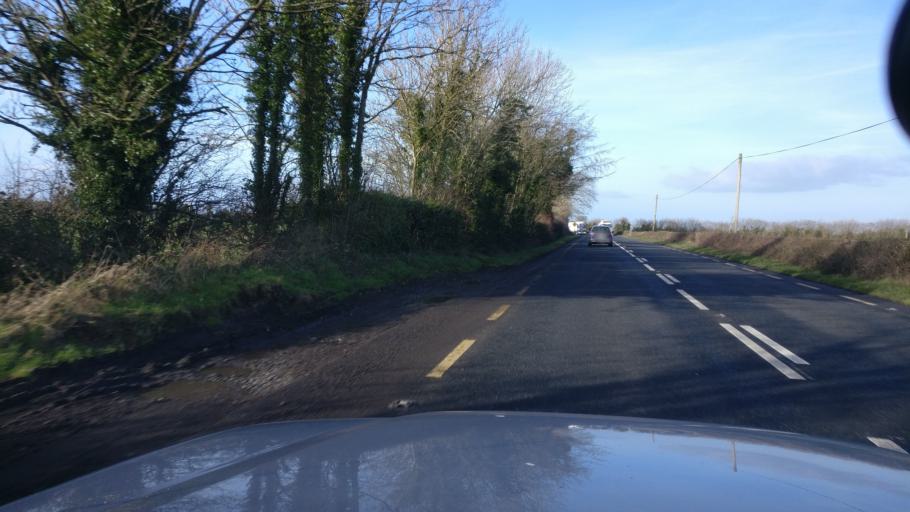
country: IE
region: Leinster
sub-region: Uibh Fhaili
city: Tullamore
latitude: 53.2036
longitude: -7.4334
